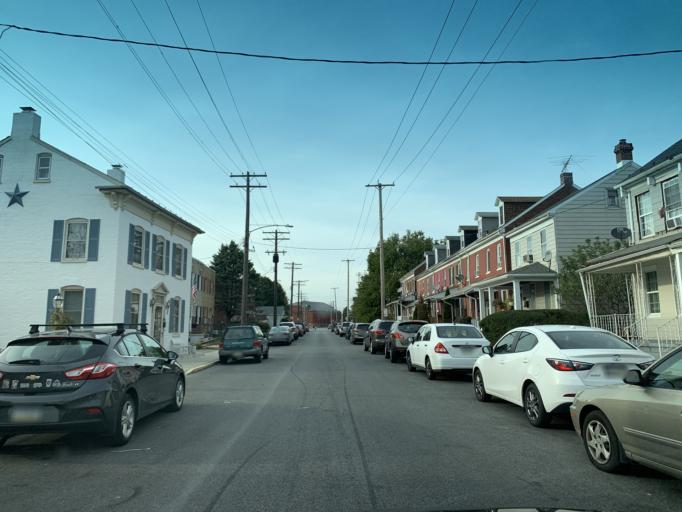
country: US
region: Pennsylvania
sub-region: York County
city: North York
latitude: 39.9692
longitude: -76.7382
